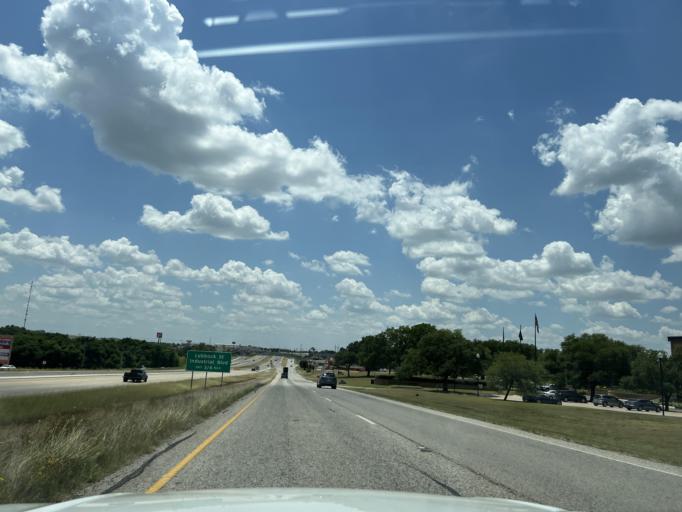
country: US
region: Texas
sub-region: Washington County
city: Brenham
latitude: 30.1428
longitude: -96.3845
